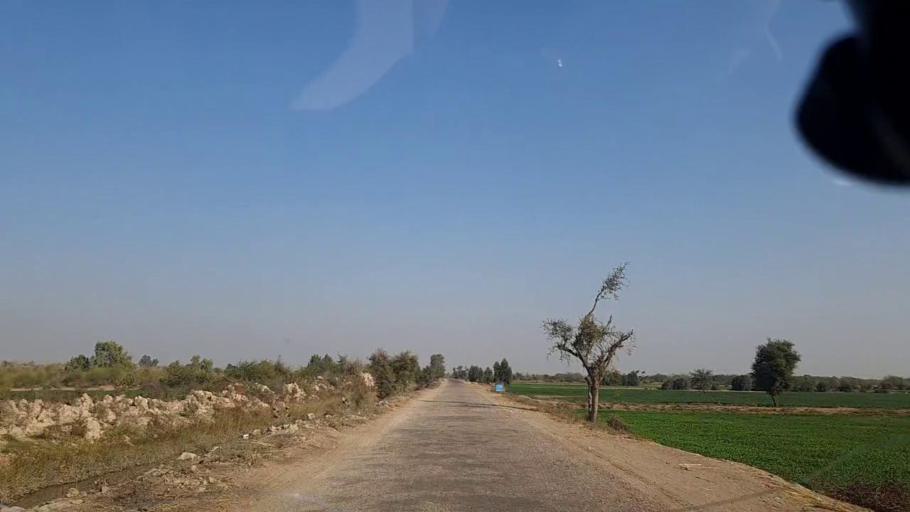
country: PK
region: Sindh
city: Khanpur
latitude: 27.6819
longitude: 69.5400
